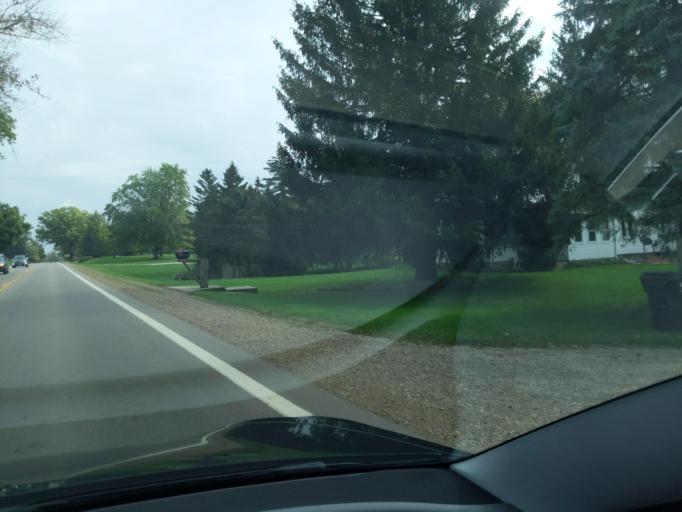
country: US
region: Michigan
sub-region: Eaton County
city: Eaton Rapids
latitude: 42.5195
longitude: -84.6770
